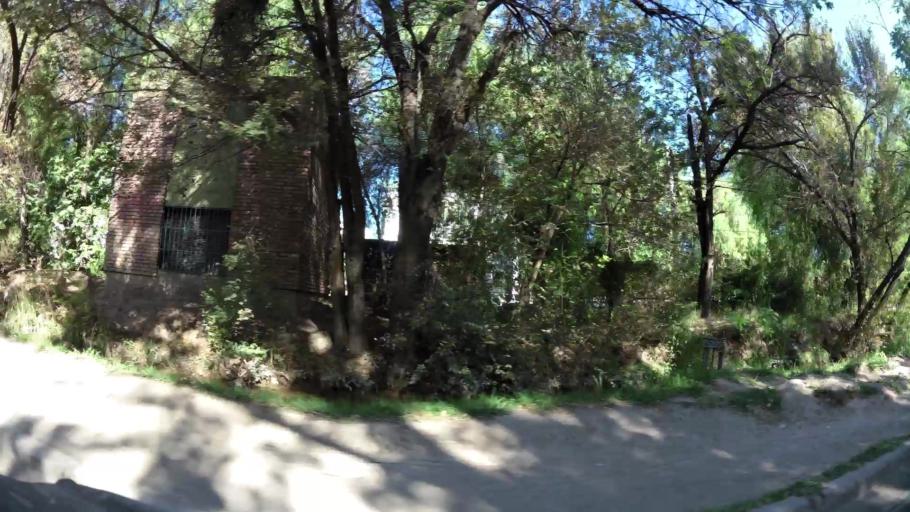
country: AR
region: Mendoza
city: Mendoza
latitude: -32.8828
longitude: -68.8735
